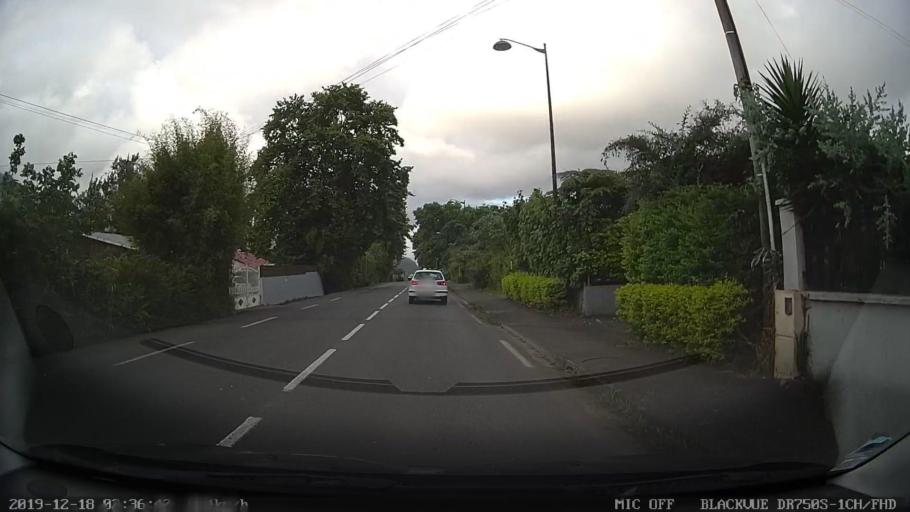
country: RE
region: Reunion
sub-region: Reunion
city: Salazie
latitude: -21.1415
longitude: 55.6218
